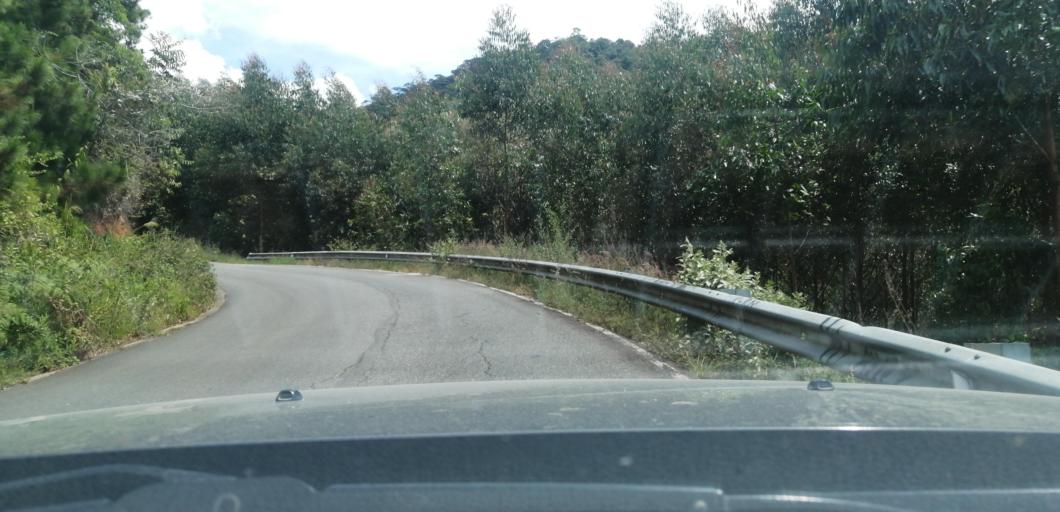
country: CO
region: Valle del Cauca
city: Dagua
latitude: 3.7113
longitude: -76.5845
